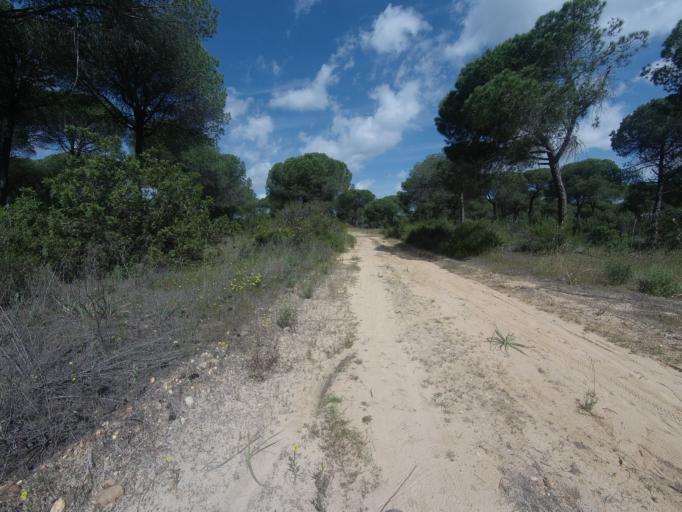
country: ES
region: Andalusia
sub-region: Provincia de Huelva
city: Aljaraque
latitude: 37.2334
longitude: -7.0618
